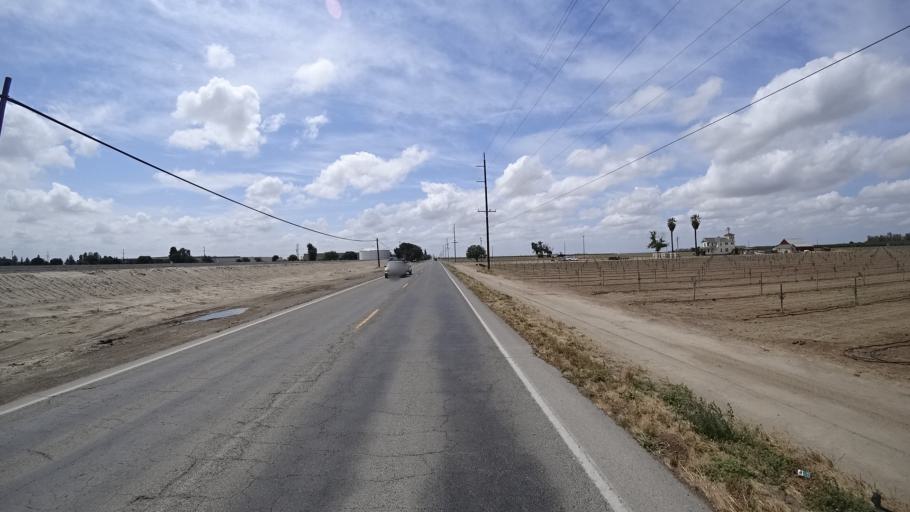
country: US
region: California
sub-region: Kings County
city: Home Garden
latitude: 36.2863
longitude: -119.6549
